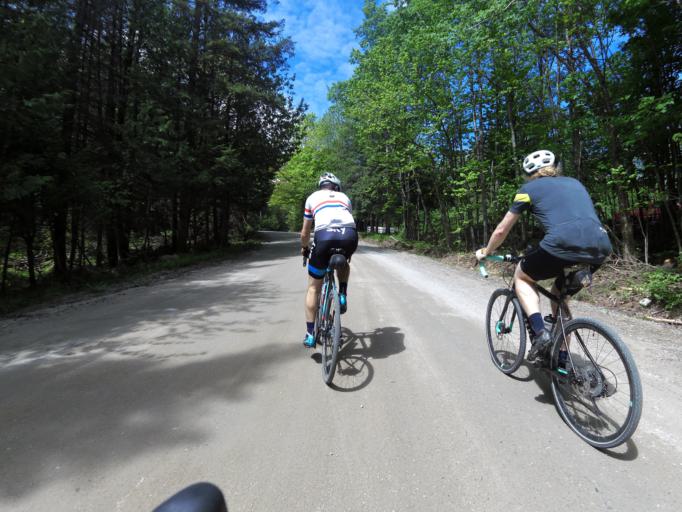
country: CA
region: Quebec
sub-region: Outaouais
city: Wakefield
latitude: 45.7846
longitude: -75.9811
